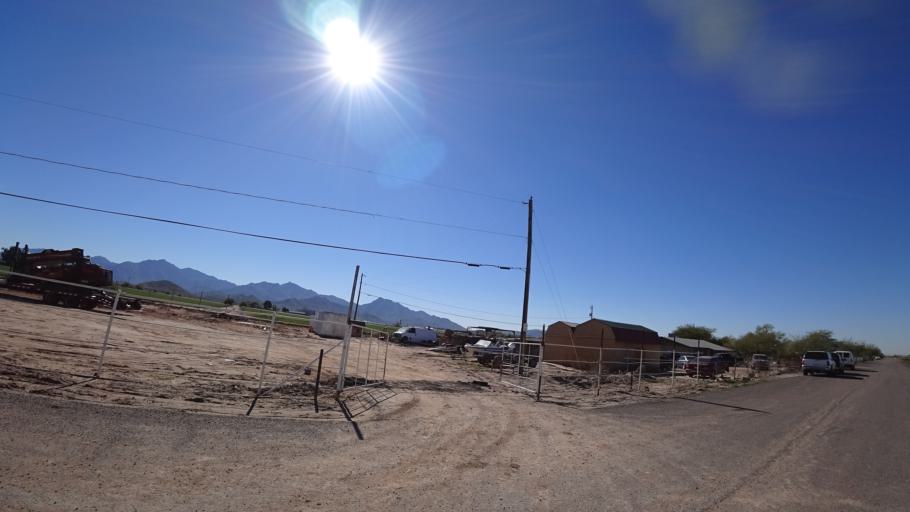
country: US
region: Arizona
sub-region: Maricopa County
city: Avondale
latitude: 33.3958
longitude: -112.3101
